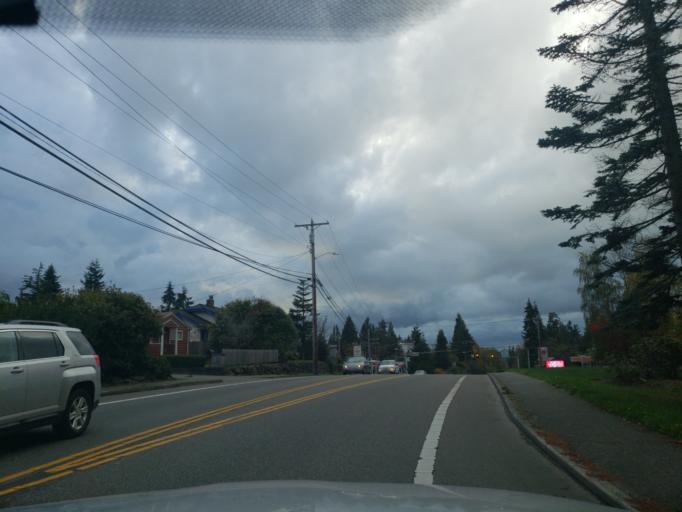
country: US
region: Washington
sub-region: Snohomish County
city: Everett
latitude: 47.9568
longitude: -122.2299
